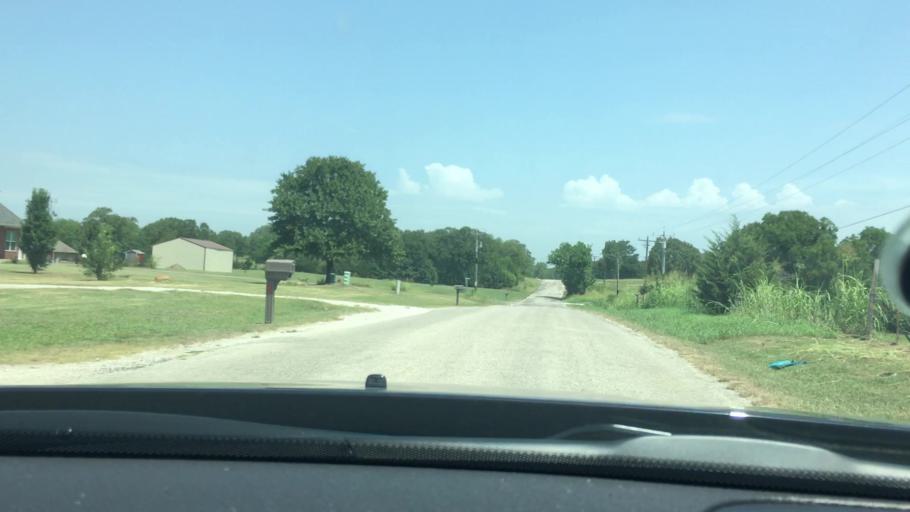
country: US
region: Oklahoma
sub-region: Pontotoc County
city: Byng
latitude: 34.8451
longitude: -96.6697
